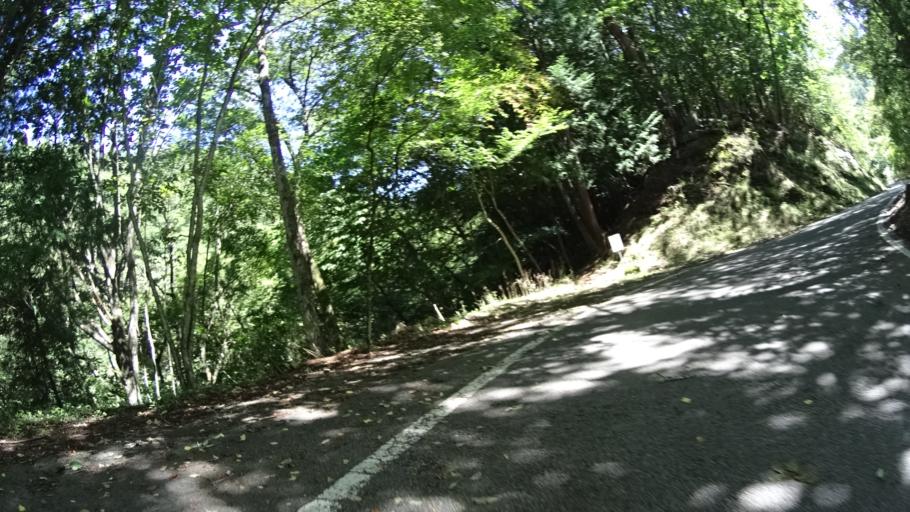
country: JP
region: Yamanashi
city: Enzan
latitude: 35.7400
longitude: 138.8104
